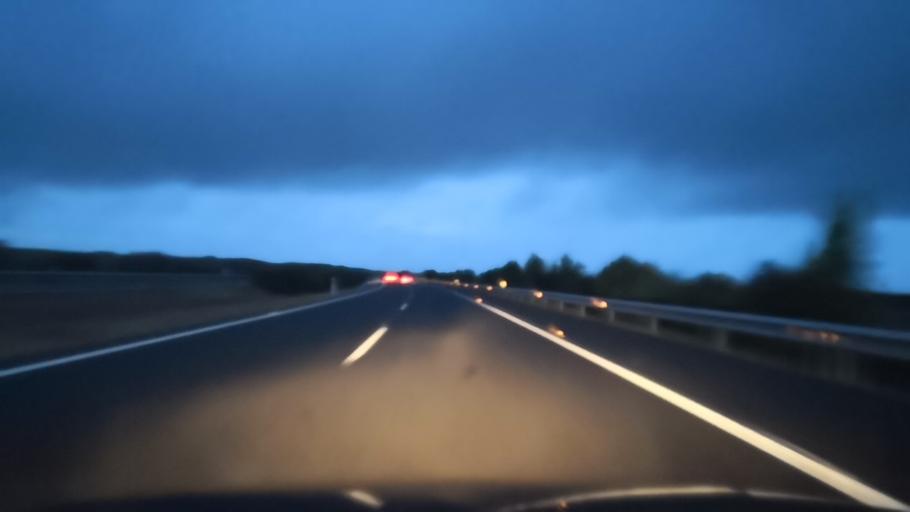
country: ES
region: Extremadura
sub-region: Provincia de Caceres
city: Aldea del Cano
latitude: 39.3324
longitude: -6.3324
